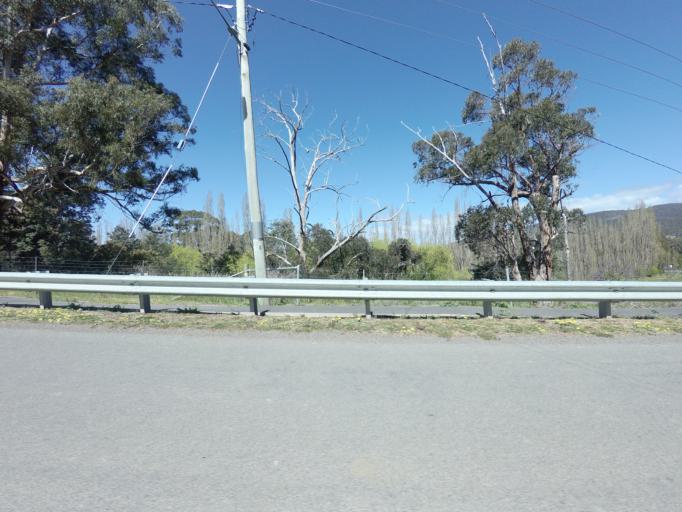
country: AU
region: Tasmania
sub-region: Derwent Valley
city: New Norfolk
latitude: -42.6711
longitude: 146.7897
